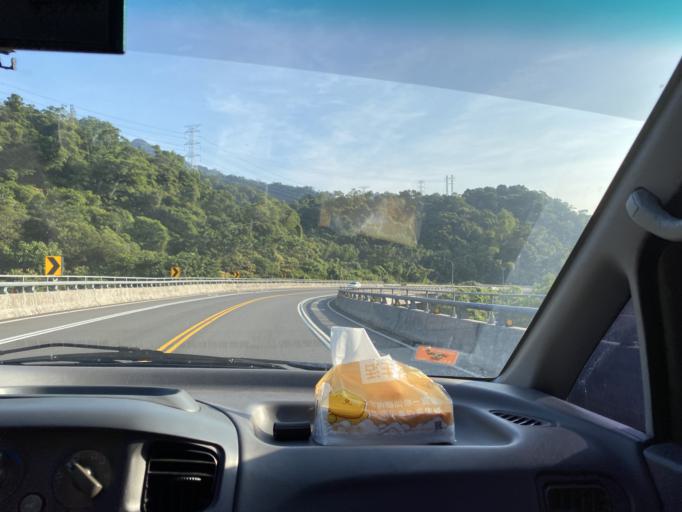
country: TW
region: Taiwan
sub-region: Keelung
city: Keelung
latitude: 25.0180
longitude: 121.8024
